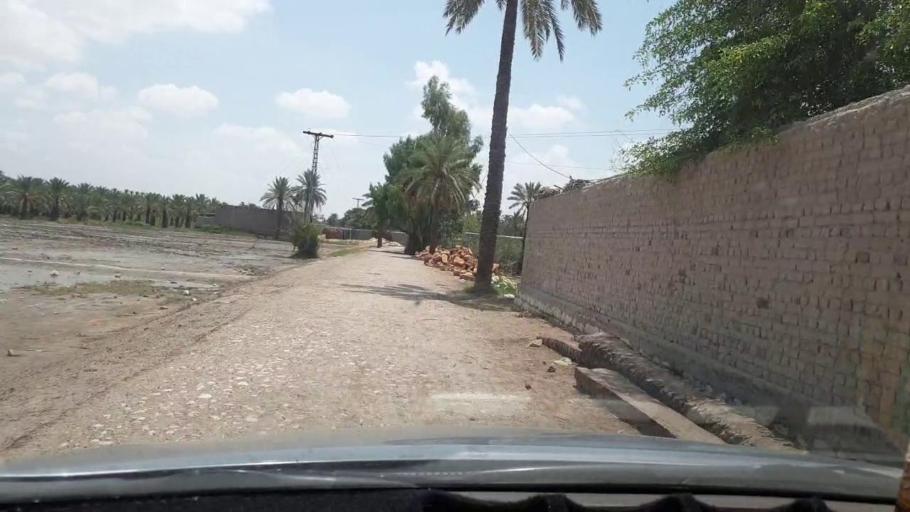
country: PK
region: Sindh
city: Khairpur
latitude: 27.4436
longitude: 68.7919
